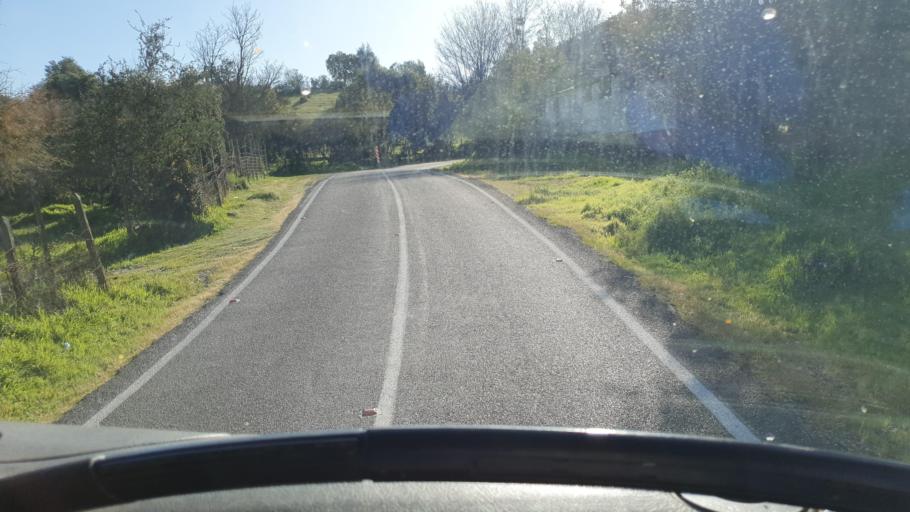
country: CL
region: Valparaiso
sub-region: Provincia de Marga Marga
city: Limache
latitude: -33.1989
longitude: -71.2276
